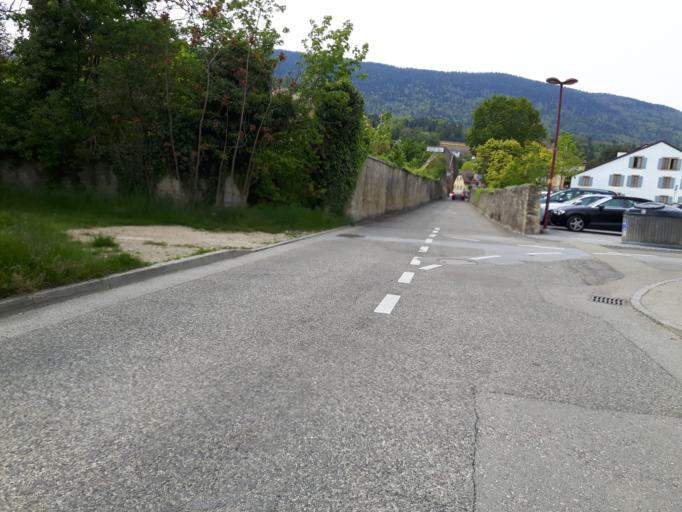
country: CH
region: Neuchatel
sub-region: Boudry District
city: Bevaix
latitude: 46.9291
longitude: 6.8160
